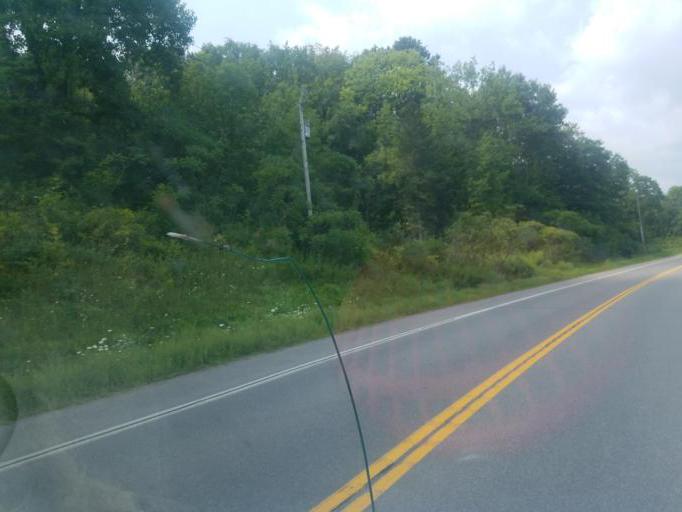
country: US
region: New York
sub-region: Herkimer County
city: Herkimer
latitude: 43.0129
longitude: -74.9447
